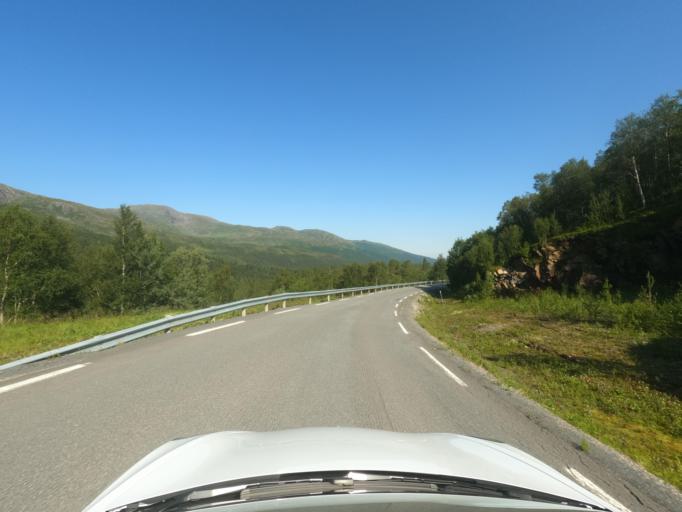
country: NO
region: Troms
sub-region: Skanland
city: Evenskjer
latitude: 68.3297
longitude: 16.5437
